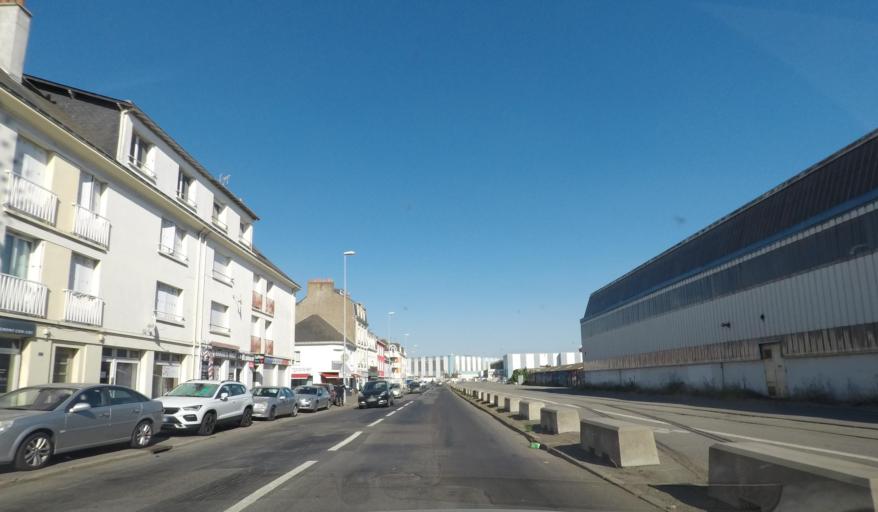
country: FR
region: Pays de la Loire
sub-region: Departement de la Loire-Atlantique
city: Saint-Nazaire
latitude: 47.2902
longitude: -2.1964
